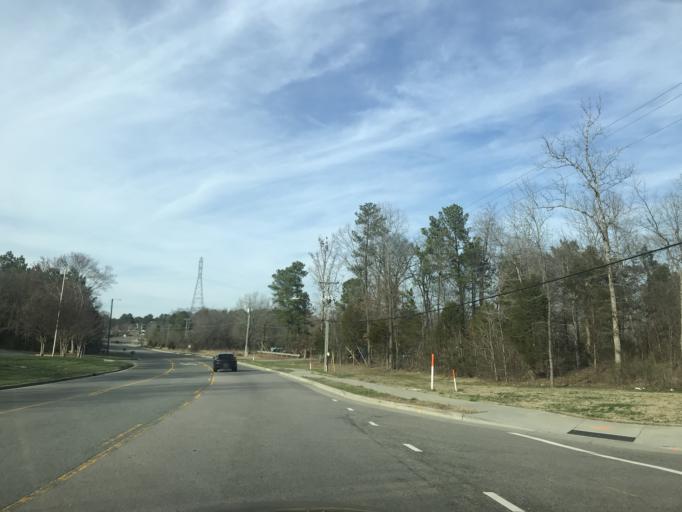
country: US
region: North Carolina
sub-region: Durham County
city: Durham
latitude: 35.9078
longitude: -78.8882
